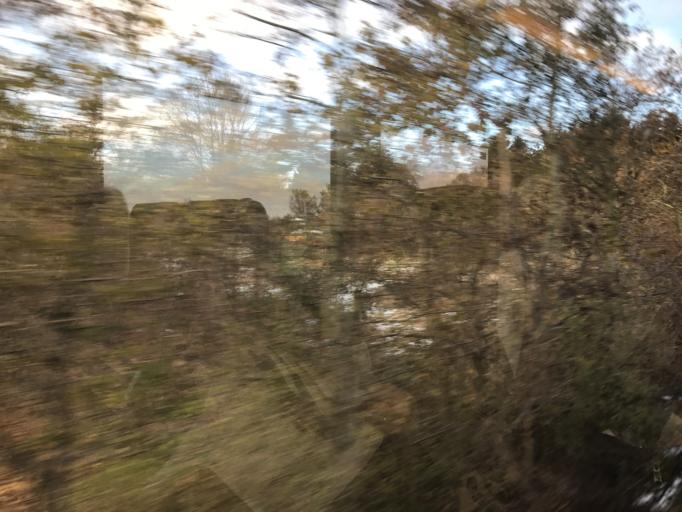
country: DK
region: Zealand
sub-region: Stevns Kommune
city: Harlev
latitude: 55.3737
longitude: 12.2131
